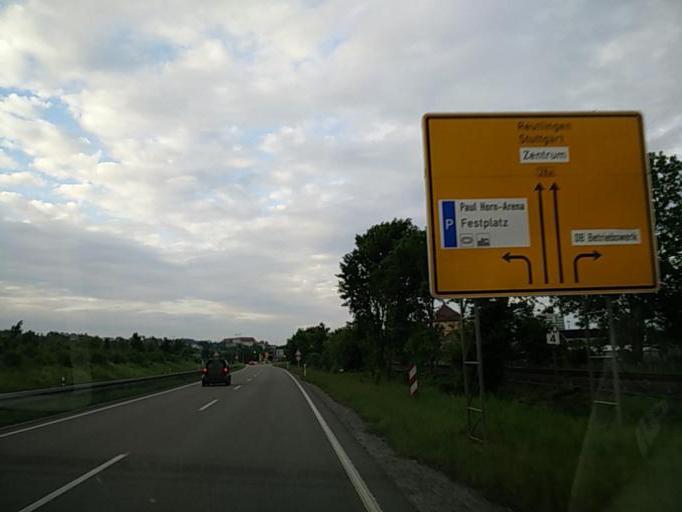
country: DE
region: Baden-Wuerttemberg
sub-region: Tuebingen Region
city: Tuebingen
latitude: 48.5063
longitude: 9.0396
